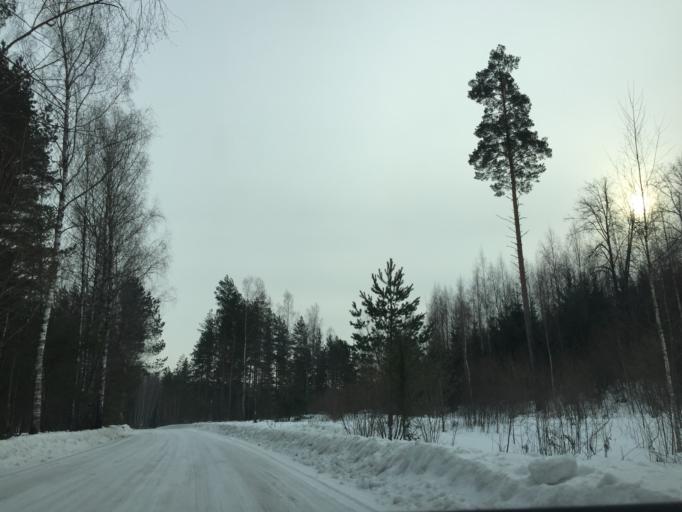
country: LV
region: Ogre
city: Ogre
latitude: 56.8406
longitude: 24.5683
